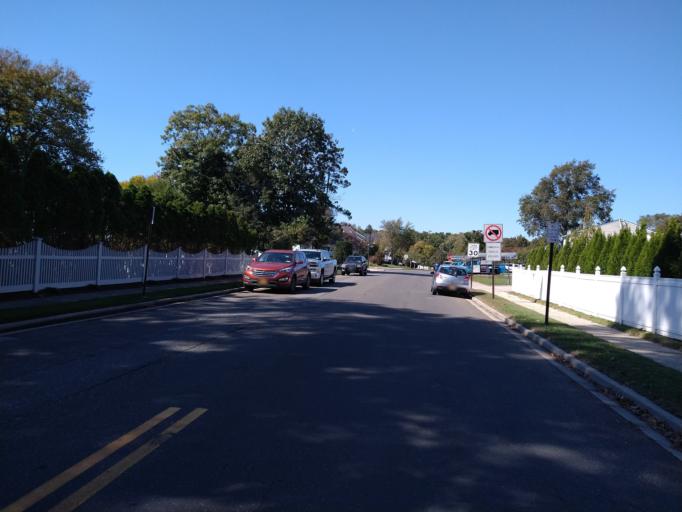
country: US
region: New York
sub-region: Nassau County
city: Syosset
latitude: 40.8323
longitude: -73.4939
